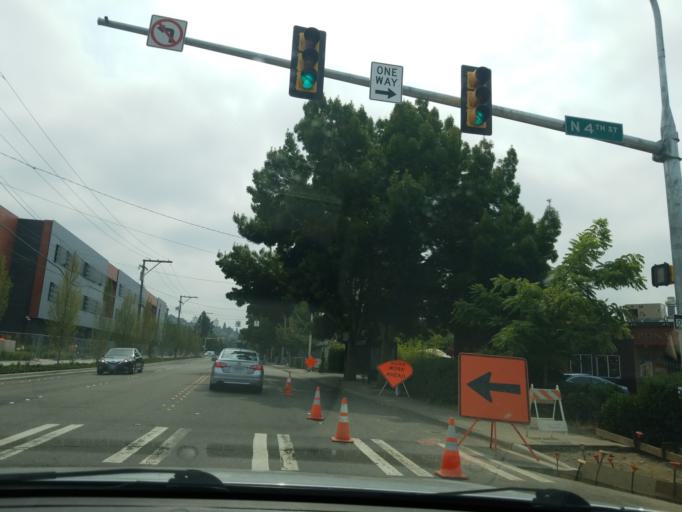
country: US
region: Washington
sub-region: King County
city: Renton
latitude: 47.4885
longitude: -122.2022
